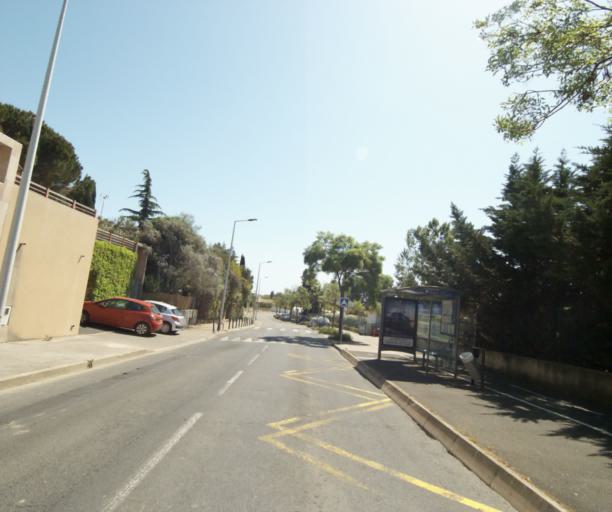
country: FR
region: Languedoc-Roussillon
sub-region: Departement de l'Herault
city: Saint-Jean-de-Vedas
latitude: 43.6022
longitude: 3.8337
